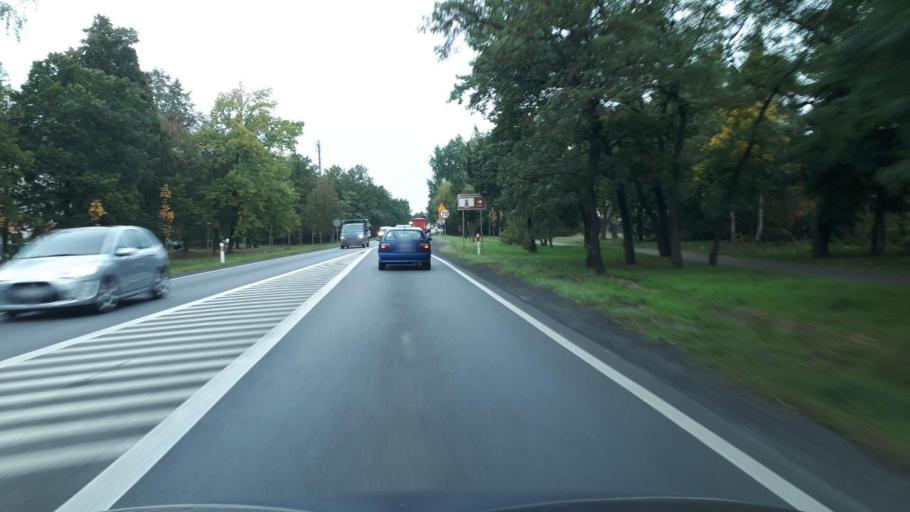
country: PL
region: Greater Poland Voivodeship
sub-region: Powiat ostrzeszowski
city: Ostrzeszow
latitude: 51.4314
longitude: 17.9185
